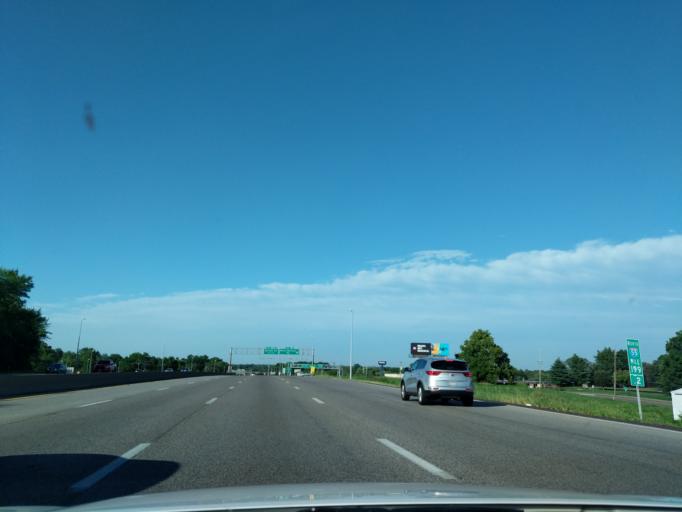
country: US
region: Missouri
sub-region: Saint Louis County
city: Saint George
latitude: 38.5302
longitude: -90.3142
